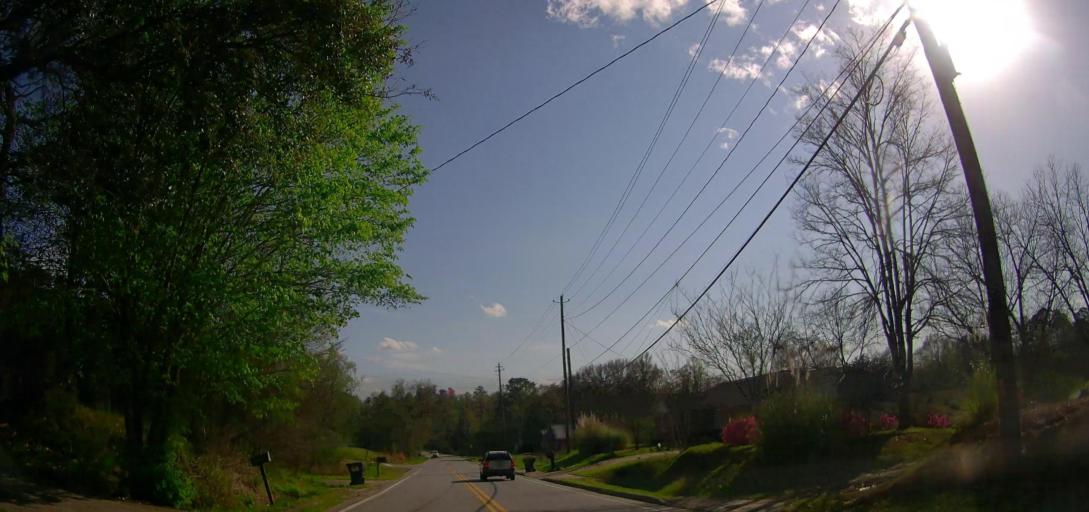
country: US
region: Georgia
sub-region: Baldwin County
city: Hardwick
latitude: 33.0508
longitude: -83.2309
